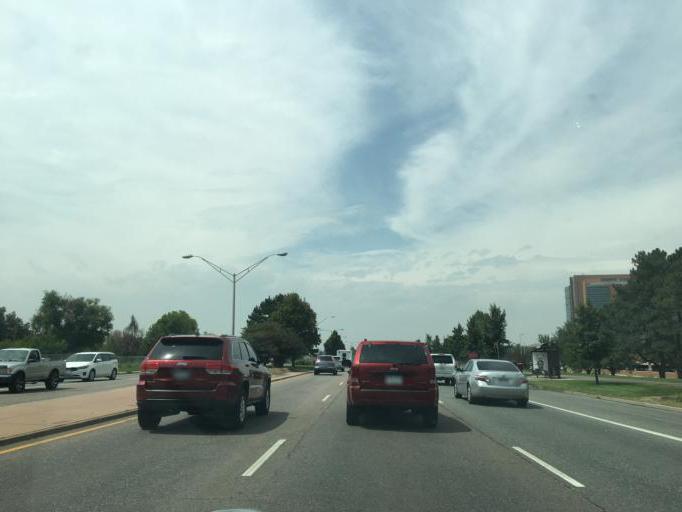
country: US
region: Colorado
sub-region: Adams County
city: Aurora
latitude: 39.7403
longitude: -104.8378
